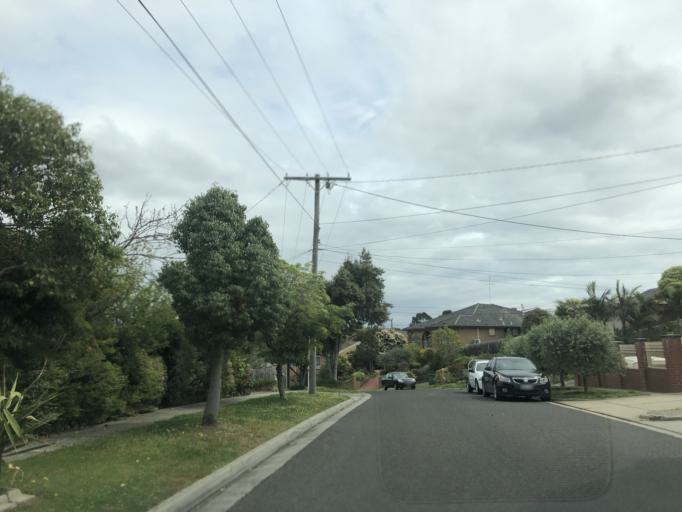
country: AU
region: Victoria
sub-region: Greater Dandenong
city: Dandenong North
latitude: -37.9453
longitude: 145.2144
